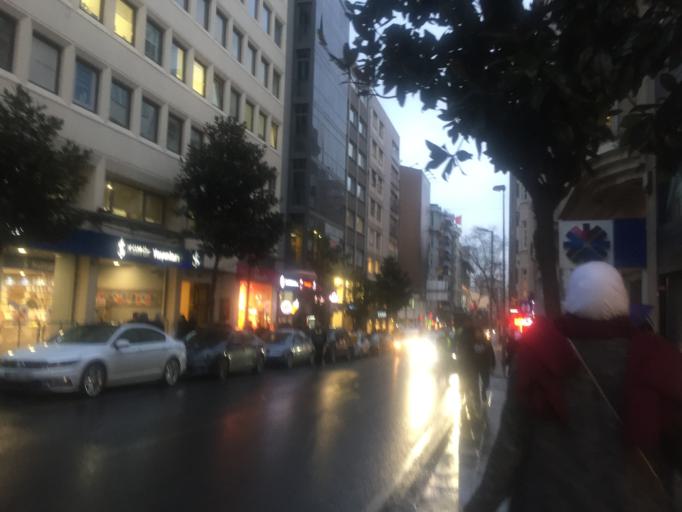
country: TR
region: Istanbul
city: Sisli
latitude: 41.0523
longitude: 28.9908
